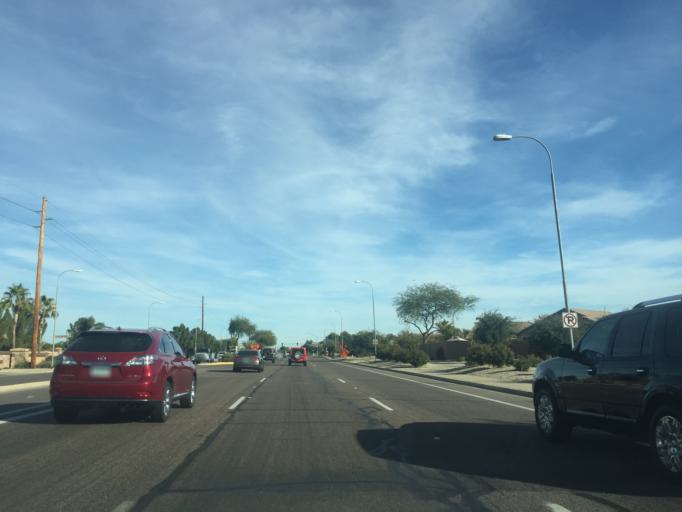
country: US
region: Arizona
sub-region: Maricopa County
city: Sun Lakes
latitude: 33.2192
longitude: -111.7670
